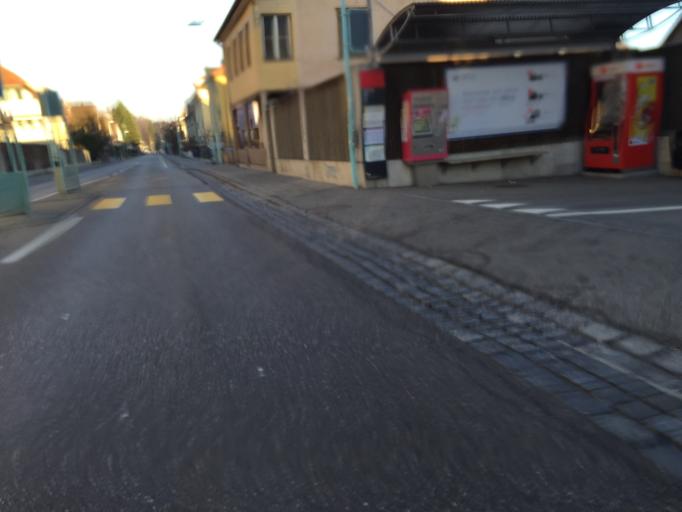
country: CH
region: Bern
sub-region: Bern-Mittelland District
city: Koniz
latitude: 46.9309
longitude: 7.4162
